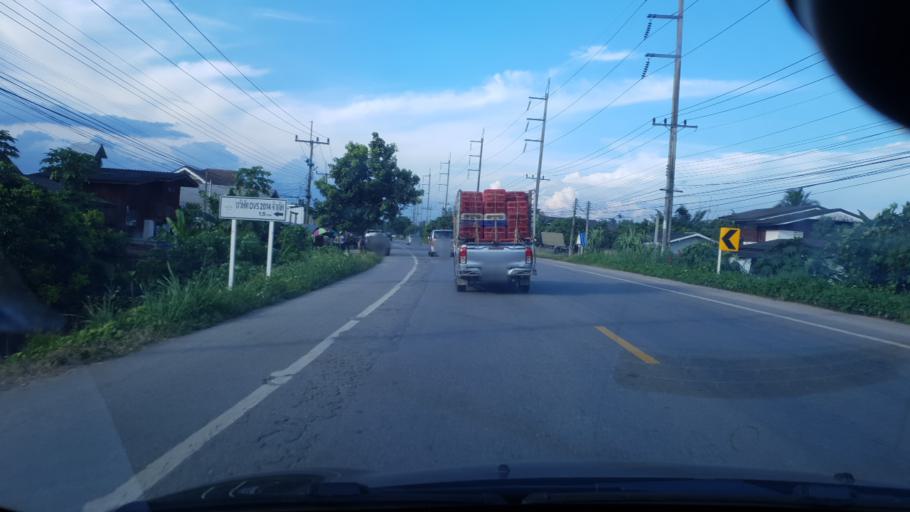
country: TH
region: Chiang Rai
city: Mae Suai
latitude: 19.5336
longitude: 99.4868
